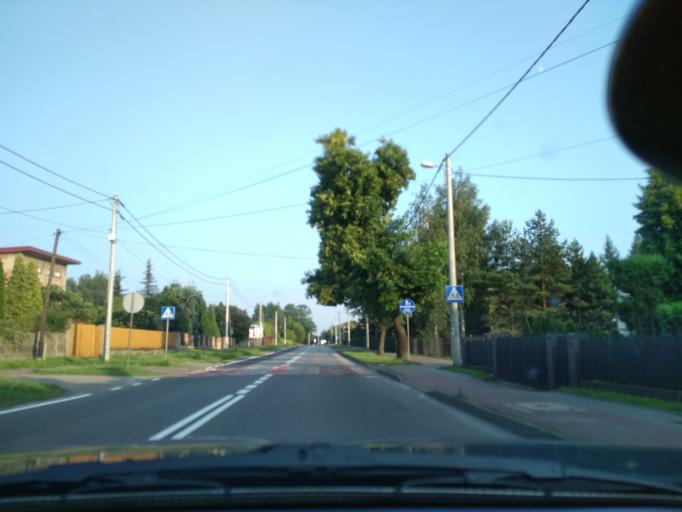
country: PL
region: Silesian Voivodeship
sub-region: Powiat zawiercianski
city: Ogrodzieniec
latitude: 50.4592
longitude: 19.4987
